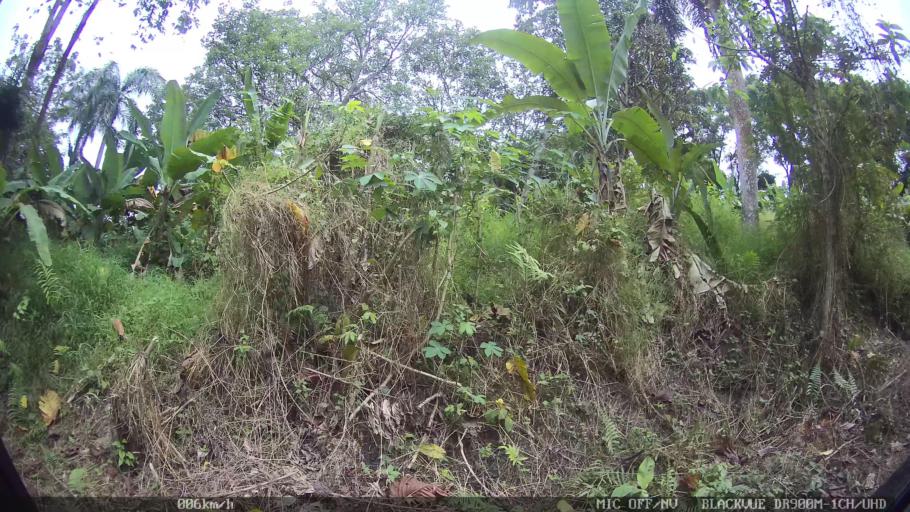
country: ID
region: Lampung
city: Panjang
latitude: -5.4314
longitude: 105.3093
